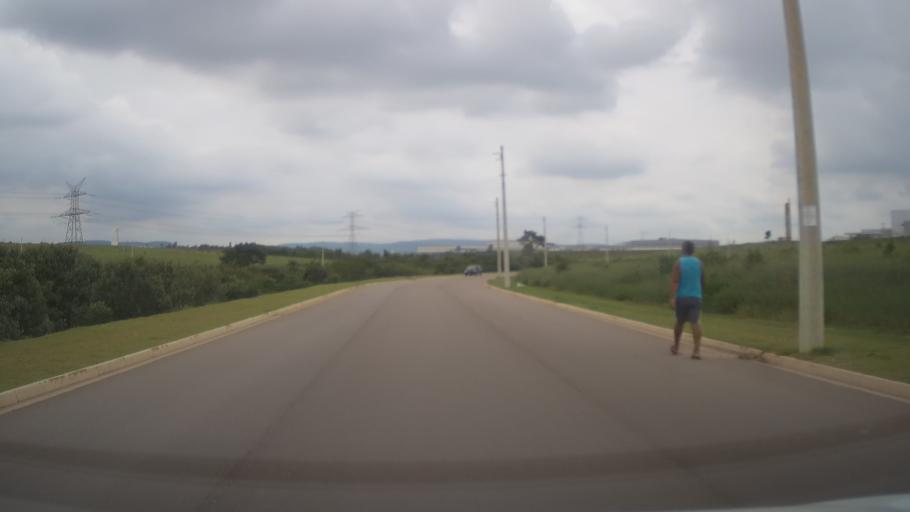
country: BR
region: Sao Paulo
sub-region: Itupeva
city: Itupeva
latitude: -23.1499
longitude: -46.9976
